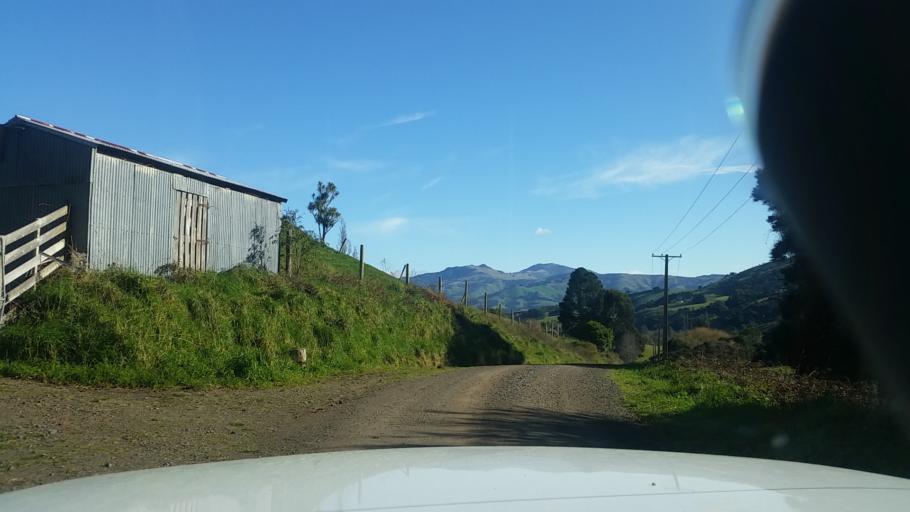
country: NZ
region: Canterbury
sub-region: Christchurch City
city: Christchurch
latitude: -43.7898
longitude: 172.9861
